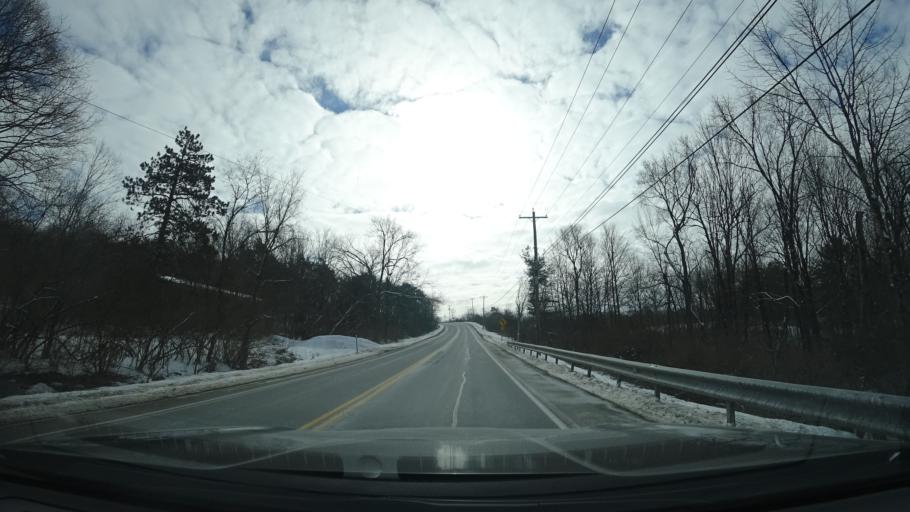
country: US
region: New York
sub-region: Washington County
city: Fort Edward
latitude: 43.2516
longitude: -73.5015
